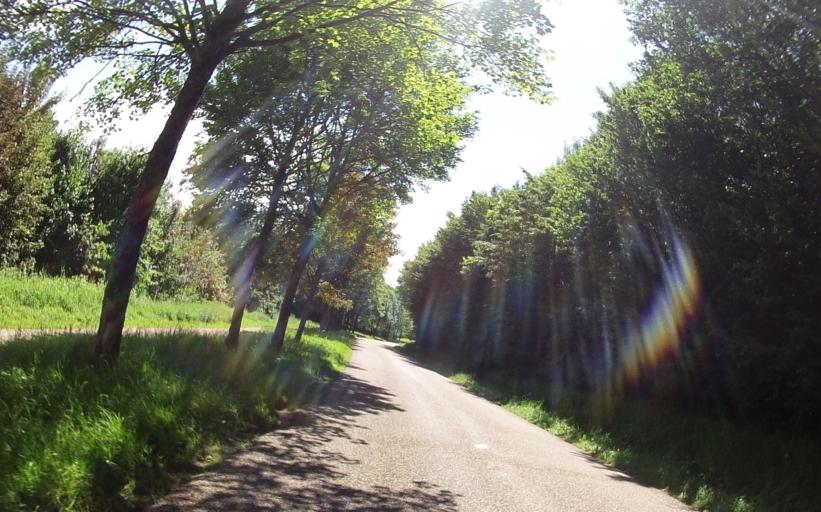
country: FR
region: Alsace
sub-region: Departement du Bas-Rhin
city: Reichshoffen
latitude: 48.9529
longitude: 7.6815
